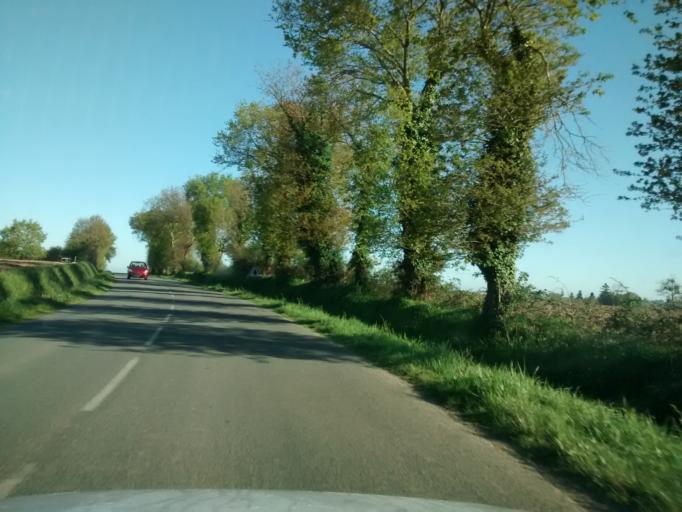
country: FR
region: Brittany
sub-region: Departement du Morbihan
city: Malestroit
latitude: 47.8198
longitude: -2.3996
